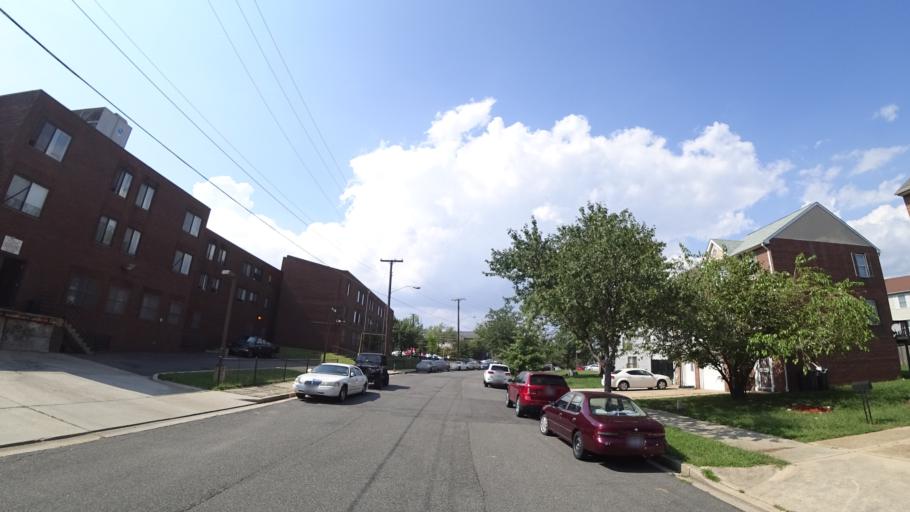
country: US
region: Maryland
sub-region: Prince George's County
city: Hillcrest Heights
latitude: 38.8522
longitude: -76.9688
